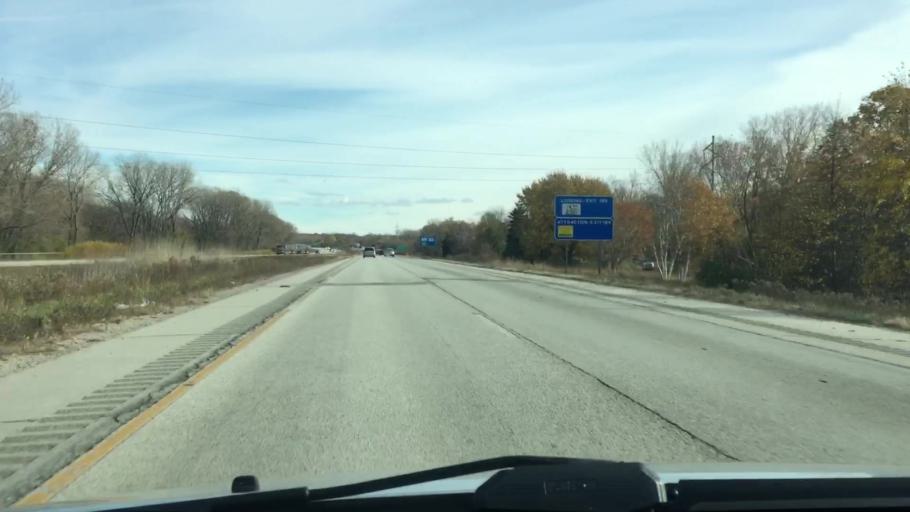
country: US
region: Wisconsin
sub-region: Brown County
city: Green Bay
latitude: 44.5233
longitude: -87.9787
